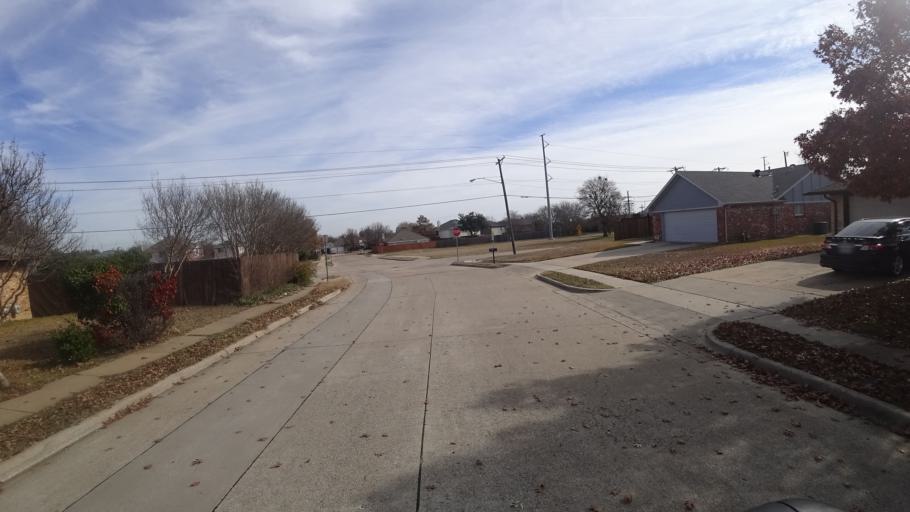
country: US
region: Texas
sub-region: Denton County
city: Highland Village
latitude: 33.0687
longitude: -97.0363
